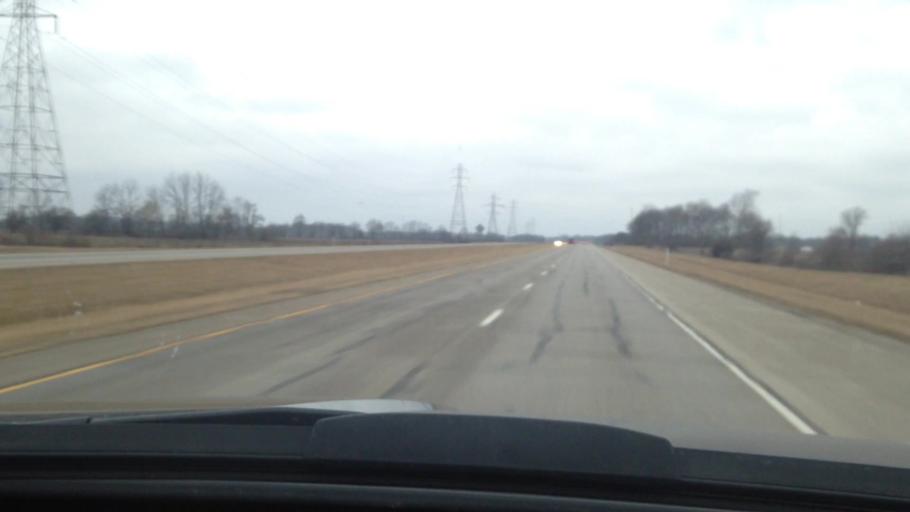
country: US
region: Indiana
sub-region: Delaware County
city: Muncie
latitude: 40.1424
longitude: -85.4066
